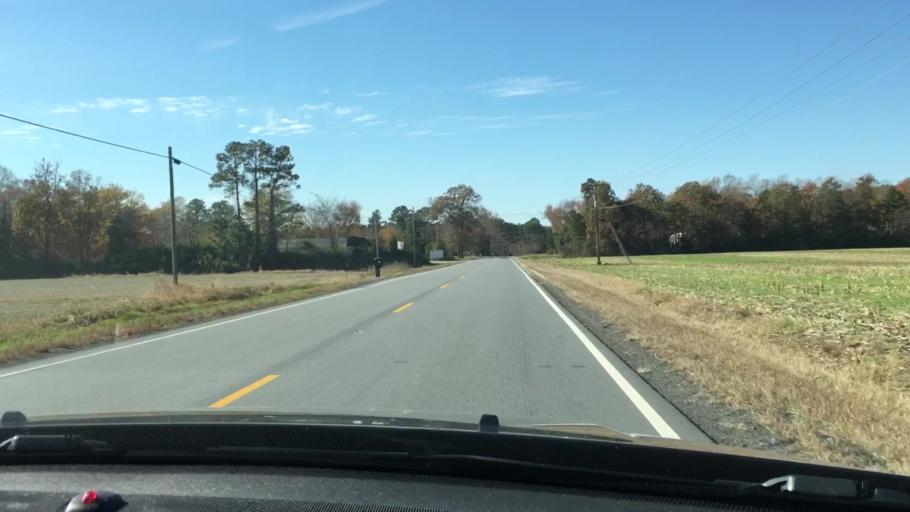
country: US
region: Virginia
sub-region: King William County
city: King William
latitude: 37.6760
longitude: -76.9917
